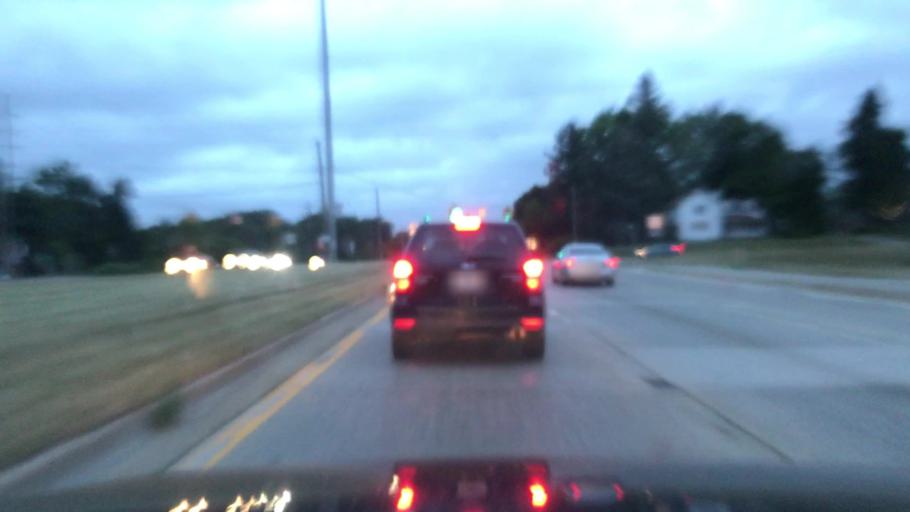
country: US
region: Michigan
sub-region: Kent County
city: East Grand Rapids
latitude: 42.9620
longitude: -85.5899
